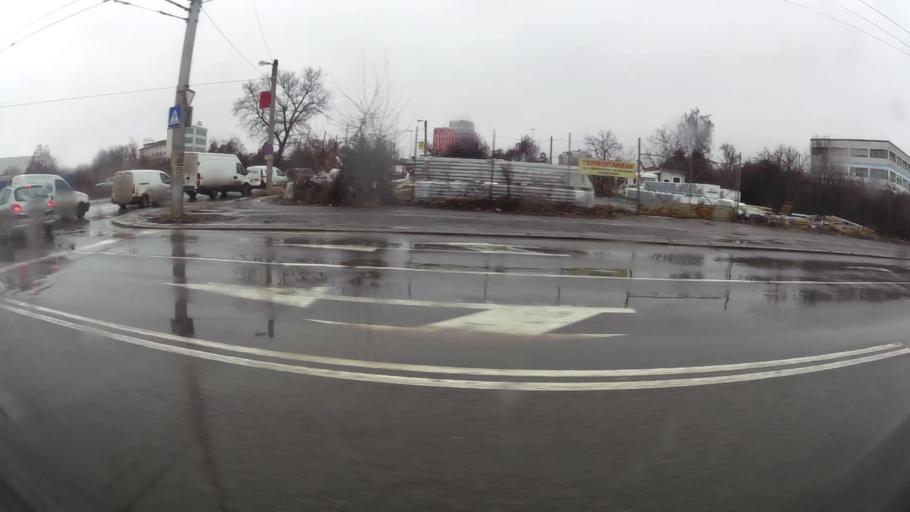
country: BG
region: Sofia-Capital
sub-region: Stolichna Obshtina
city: Sofia
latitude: 42.6404
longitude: 23.4122
